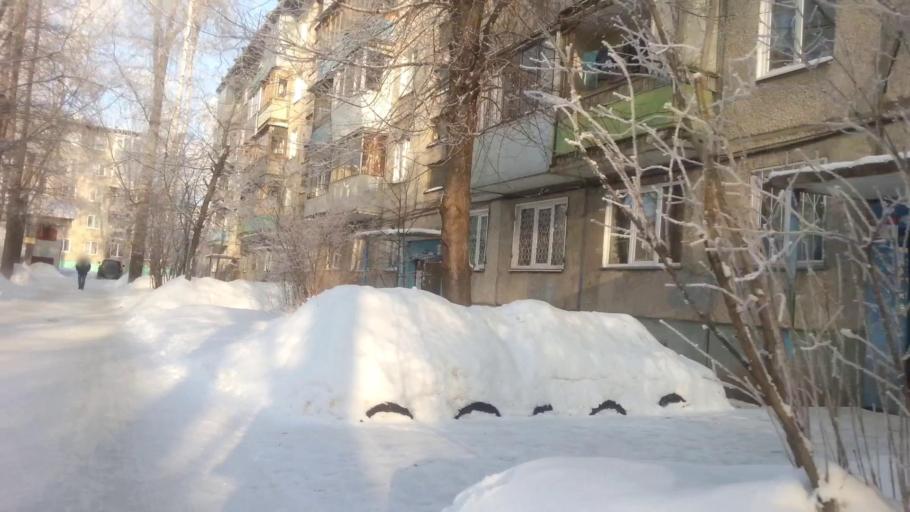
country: RU
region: Altai Krai
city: Novosilikatnyy
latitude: 53.3769
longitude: 83.6728
